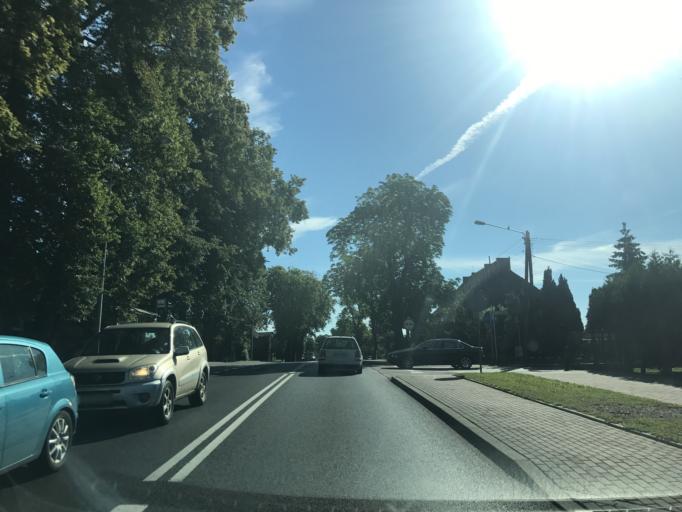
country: PL
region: Pomeranian Voivodeship
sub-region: Powiat czluchowski
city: Czluchow
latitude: 53.6743
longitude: 17.3746
